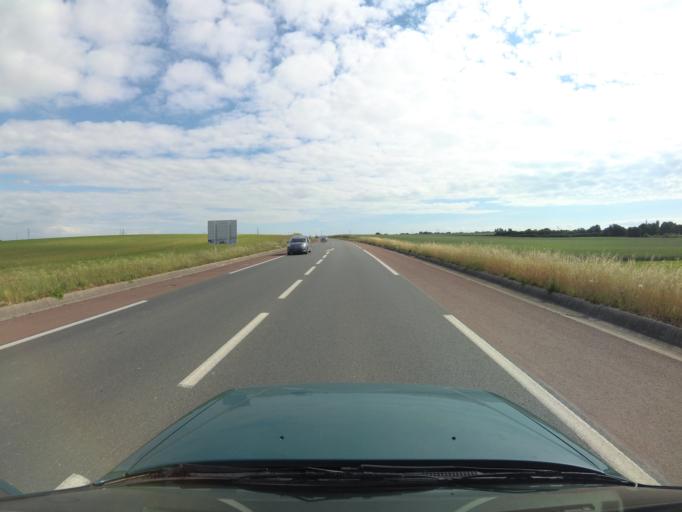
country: FR
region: Poitou-Charentes
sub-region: Departement de la Charente-Maritime
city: Saint-Xandre
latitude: 46.2147
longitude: -1.0906
